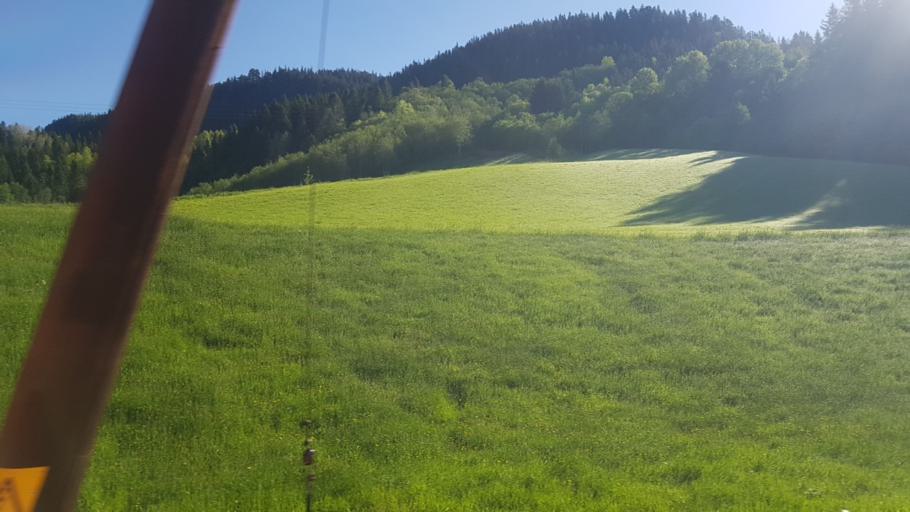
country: NO
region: Sor-Trondelag
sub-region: Melhus
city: Lundamo
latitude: 63.2179
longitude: 10.2945
